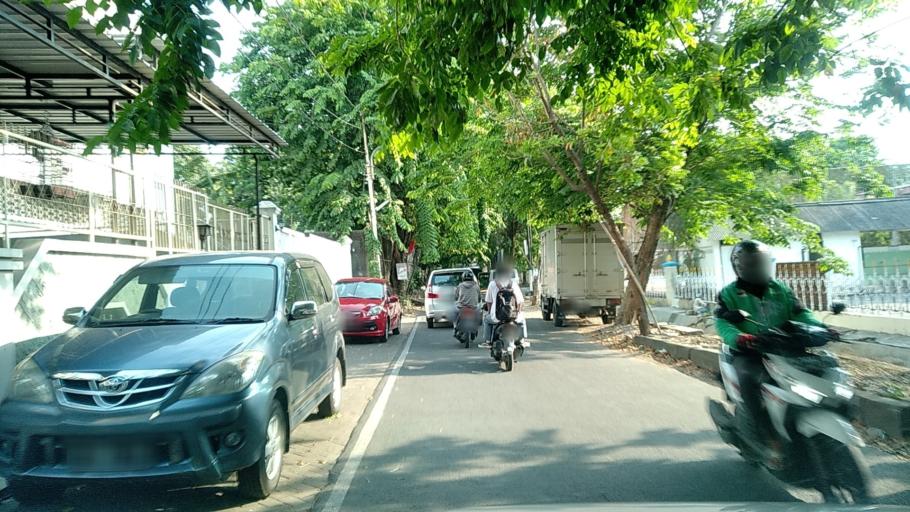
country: ID
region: Central Java
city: Semarang
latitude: -6.9995
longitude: 110.4299
